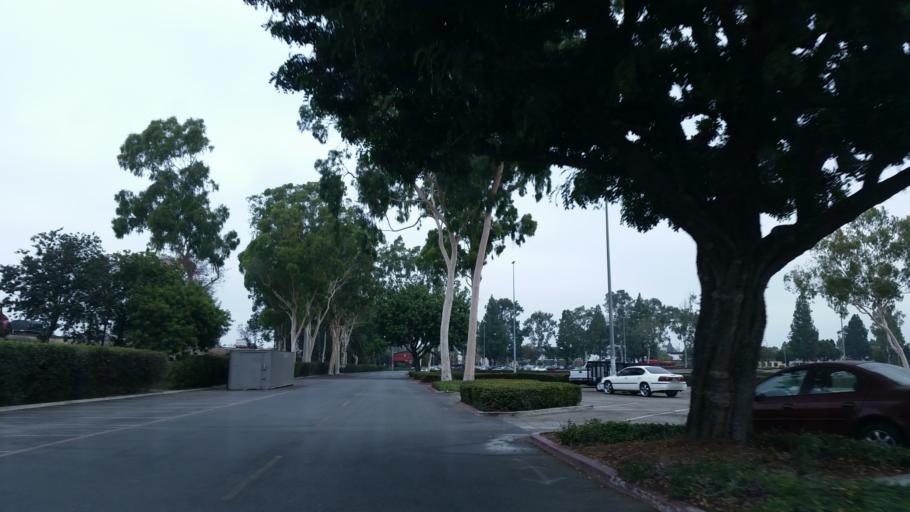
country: US
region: California
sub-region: Los Angeles County
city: Artesia
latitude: 33.8631
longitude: -118.0971
